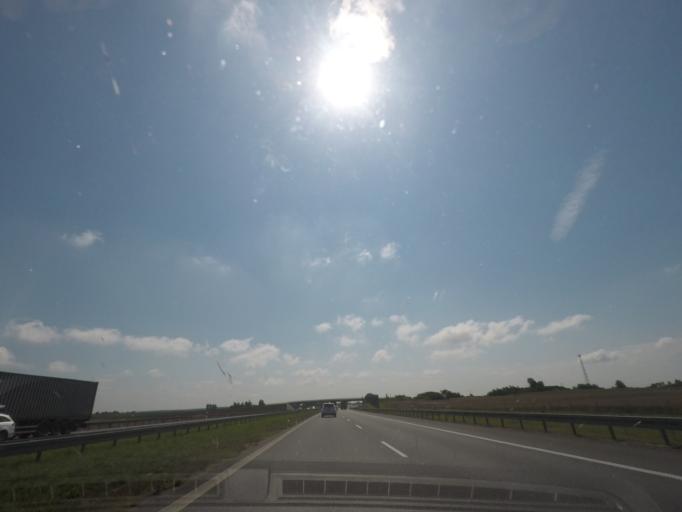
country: PL
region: Kujawsko-Pomorskie
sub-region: Powiat wloclawski
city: Kowal
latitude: 52.4782
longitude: 19.1728
